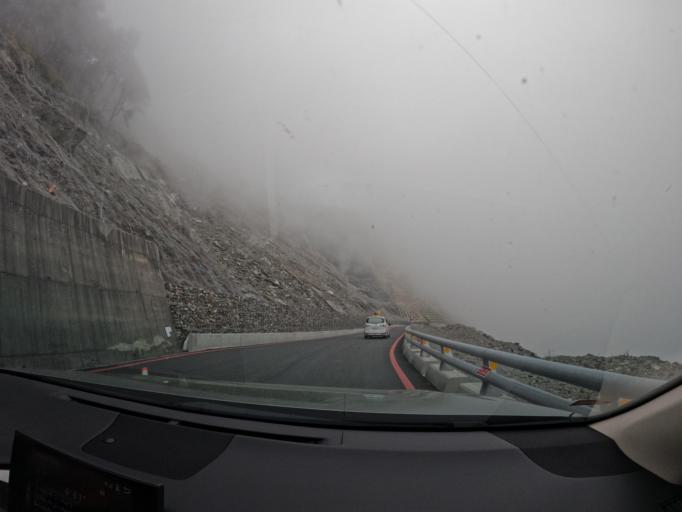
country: TW
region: Taiwan
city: Yujing
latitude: 23.2657
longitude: 120.9669
